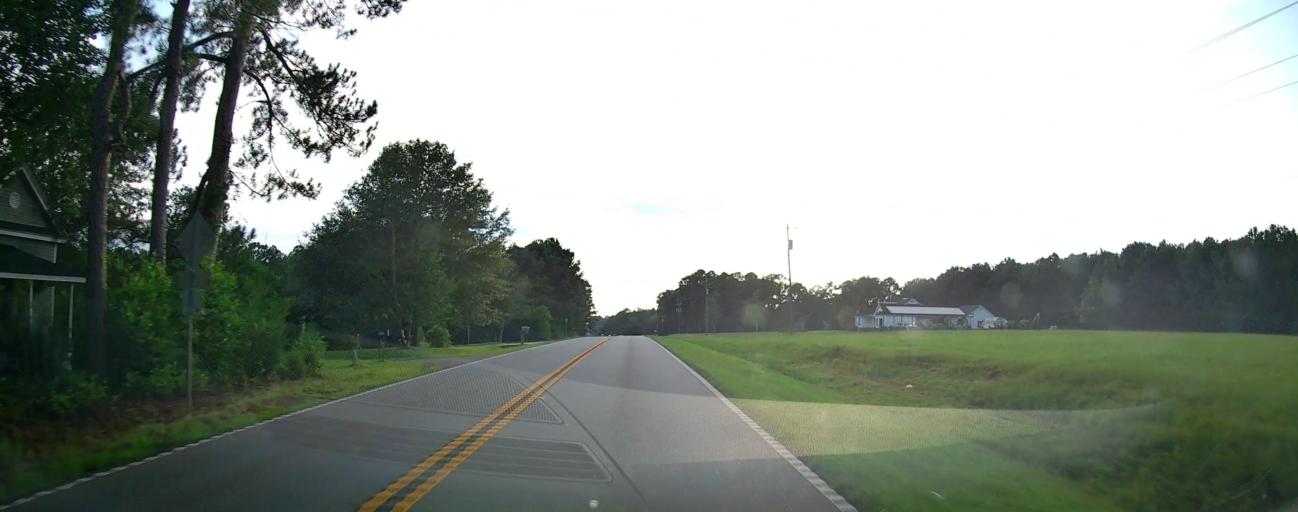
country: US
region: Georgia
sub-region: Peach County
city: Fort Valley
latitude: 32.5584
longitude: -83.9184
